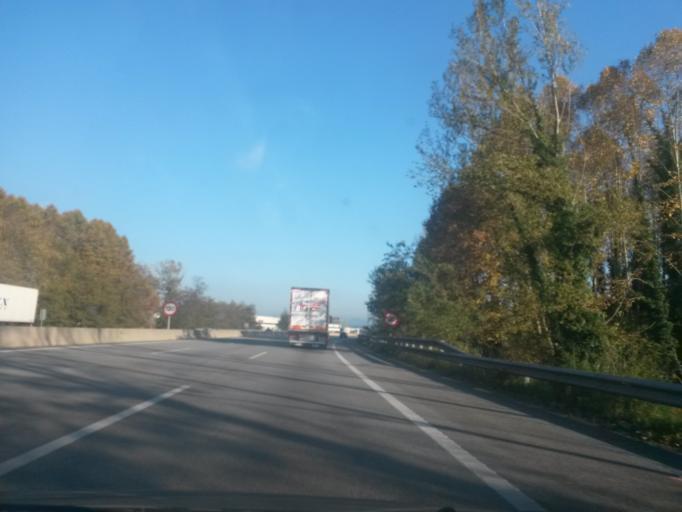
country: ES
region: Catalonia
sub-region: Provincia de Girona
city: Hostalric
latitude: 41.7421
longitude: 2.6497
